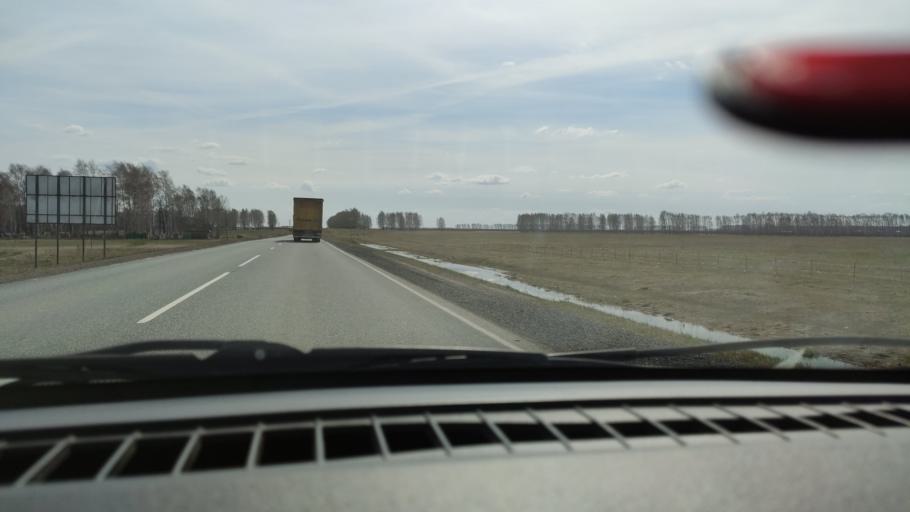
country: RU
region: Bashkortostan
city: Dyurtyuli
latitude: 55.2754
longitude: 55.0447
